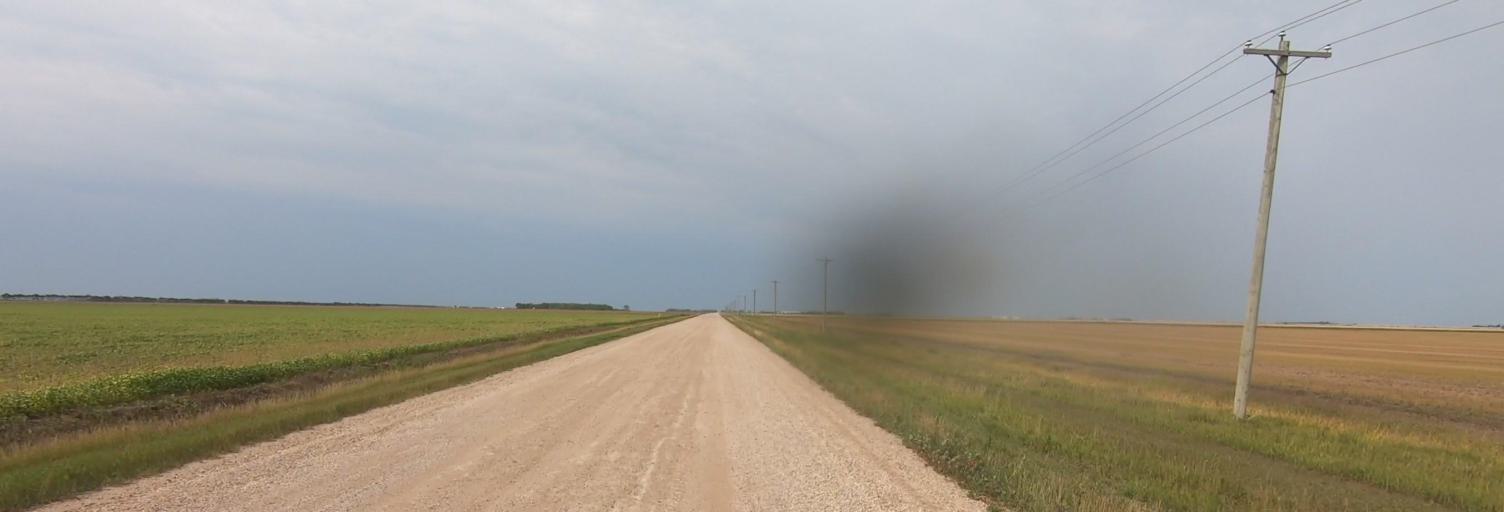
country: CA
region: Manitoba
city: Morris
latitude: 49.5765
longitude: -97.2934
